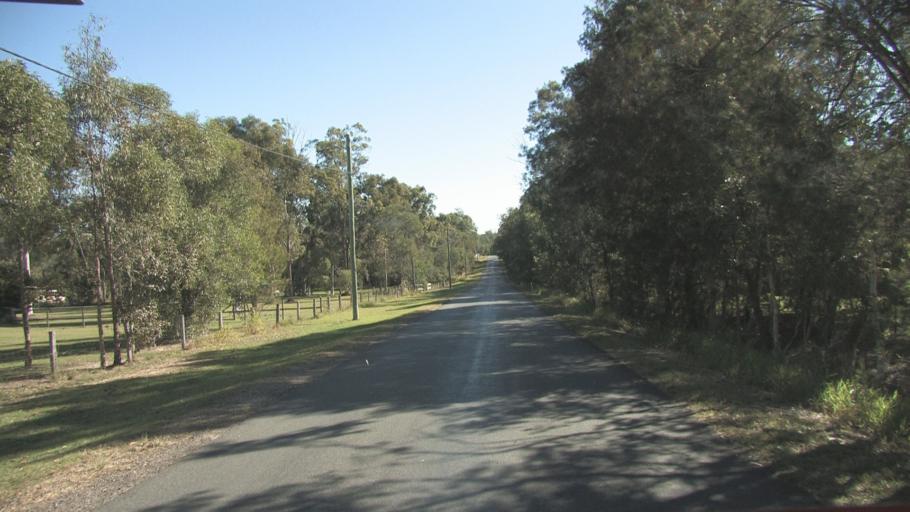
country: AU
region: Queensland
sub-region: Logan
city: Chambers Flat
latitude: -27.7344
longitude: 153.0775
